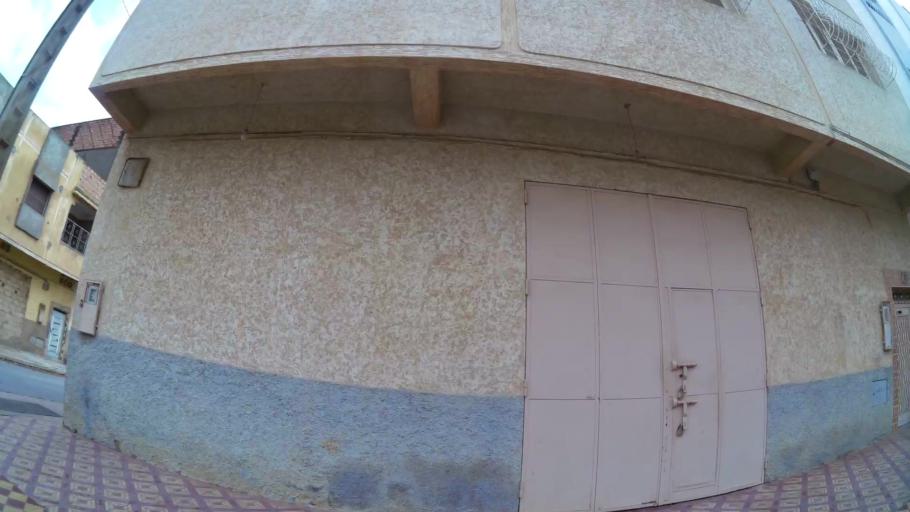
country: MA
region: Rabat-Sale-Zemmour-Zaer
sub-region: Khemisset
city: Tiflet
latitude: 33.8895
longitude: -6.3253
